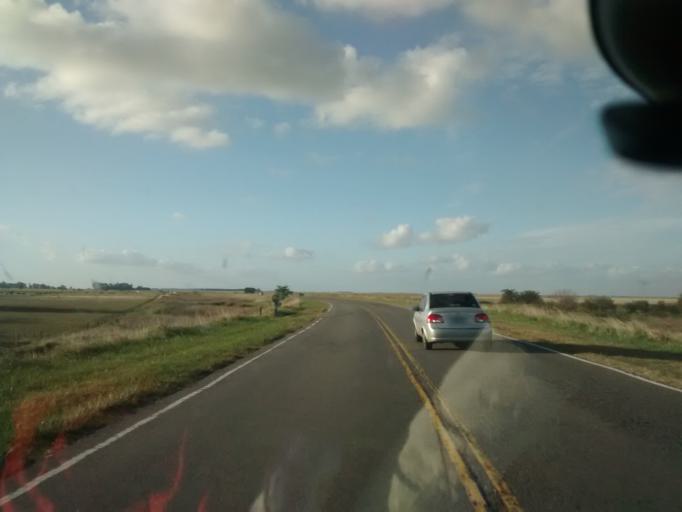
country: AR
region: Buenos Aires
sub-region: Partido de General Belgrano
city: General Belgrano
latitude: -36.1293
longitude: -58.5929
